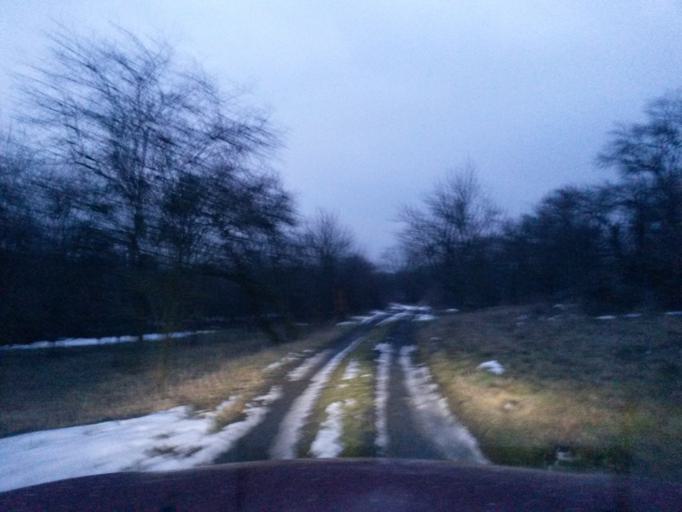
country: SK
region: Kosicky
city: Secovce
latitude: 48.7115
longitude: 21.6294
